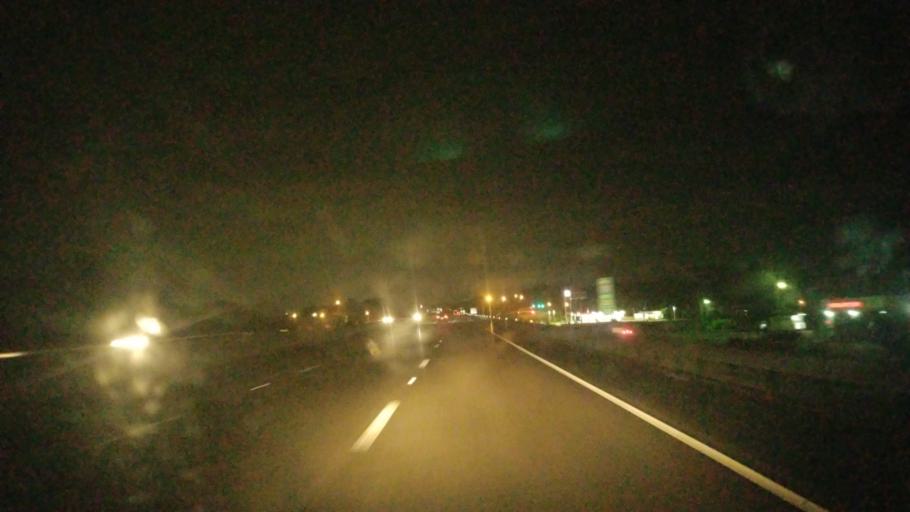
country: US
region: Missouri
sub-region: Saint Louis County
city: Spanish Lake
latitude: 38.7694
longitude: -90.2172
